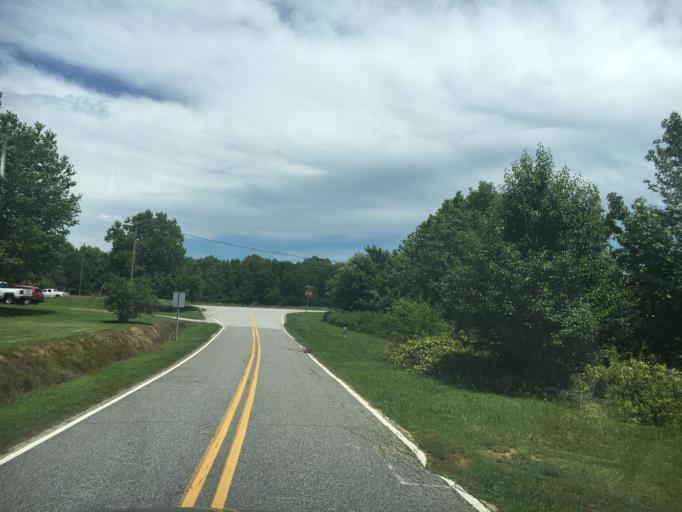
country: US
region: South Carolina
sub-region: Greenville County
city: Five Forks
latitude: 34.8470
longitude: -82.1492
